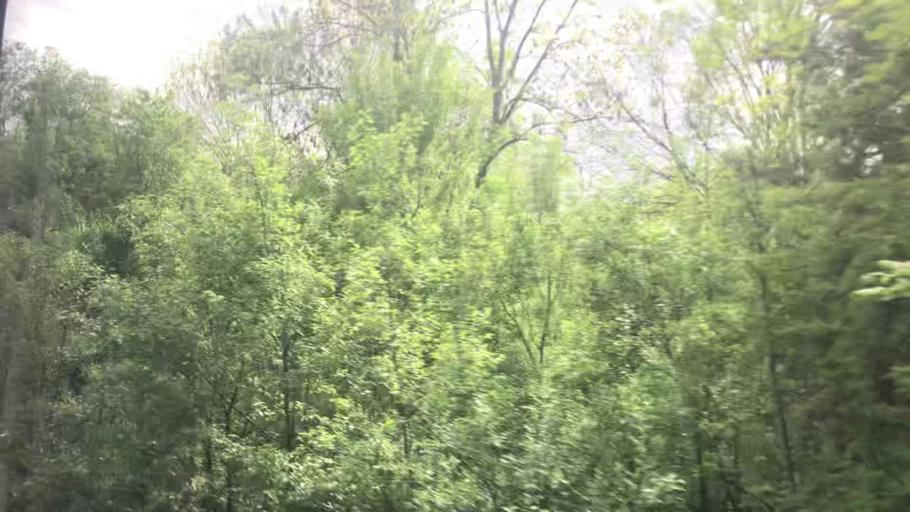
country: PL
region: Lower Silesian Voivodeship
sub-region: Powiat swidnicki
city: Swiebodzice
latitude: 50.8519
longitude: 16.3336
